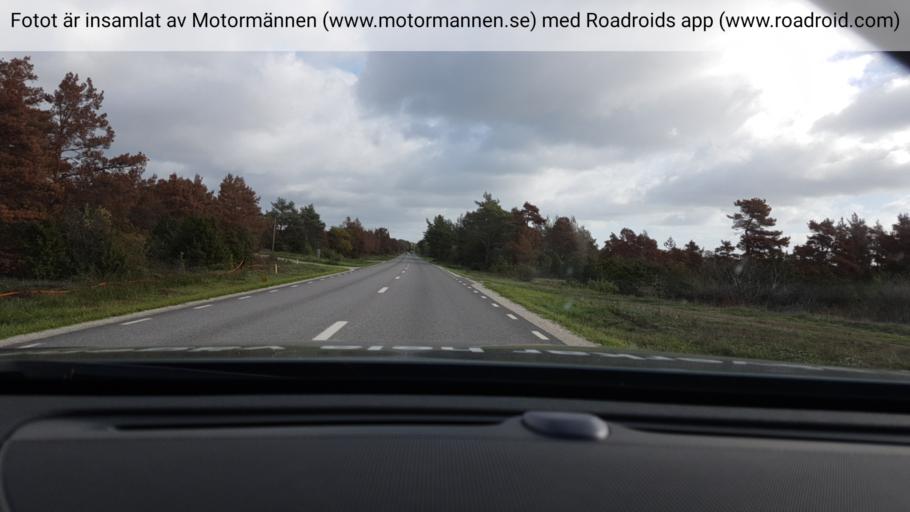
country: SE
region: Gotland
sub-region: Gotland
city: Visby
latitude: 57.6650
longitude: 18.4587
